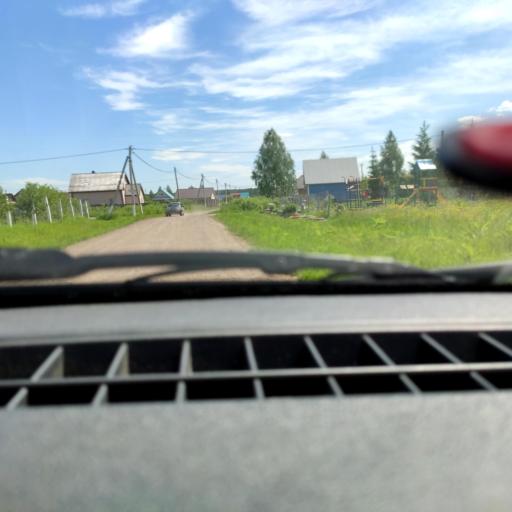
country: RU
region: Bashkortostan
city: Kabakovo
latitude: 54.7262
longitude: 56.2071
